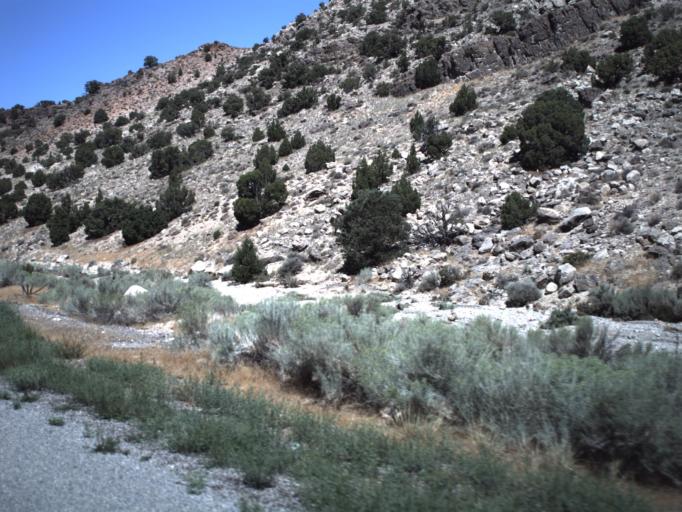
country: US
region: Utah
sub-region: Beaver County
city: Milford
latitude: 39.0836
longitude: -113.5949
